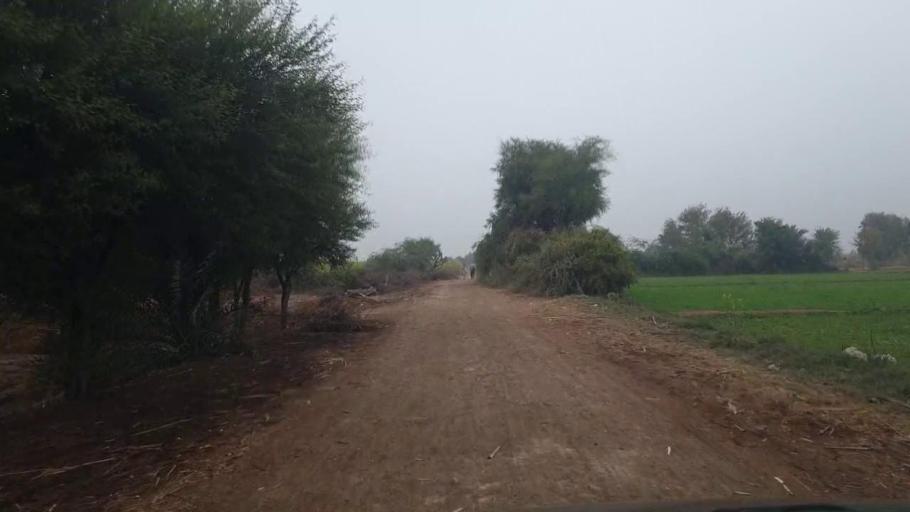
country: PK
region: Sindh
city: Tando Adam
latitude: 25.8061
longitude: 68.6865
